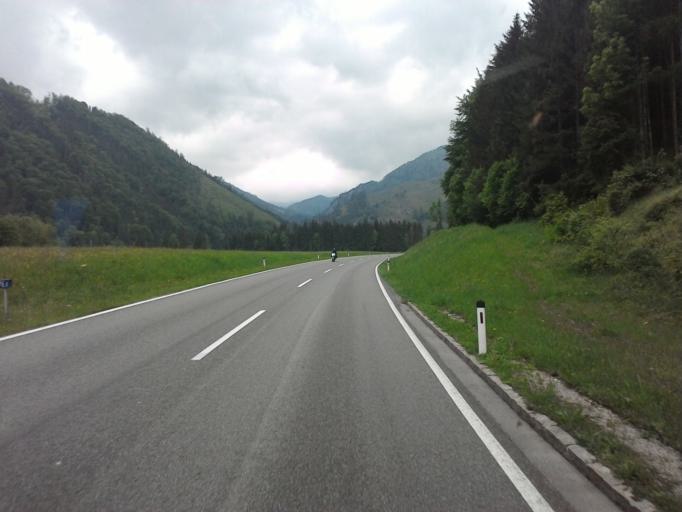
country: AT
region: Styria
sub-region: Politischer Bezirk Liezen
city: Altenmarkt bei Sankt Gallen
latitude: 47.7432
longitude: 14.6465
